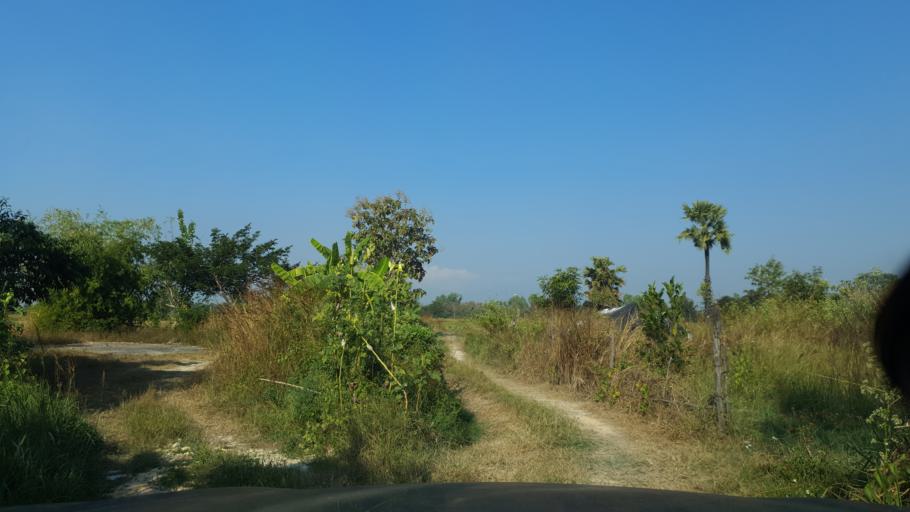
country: TH
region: Lamphun
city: Ban Thi
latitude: 18.6759
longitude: 99.1345
